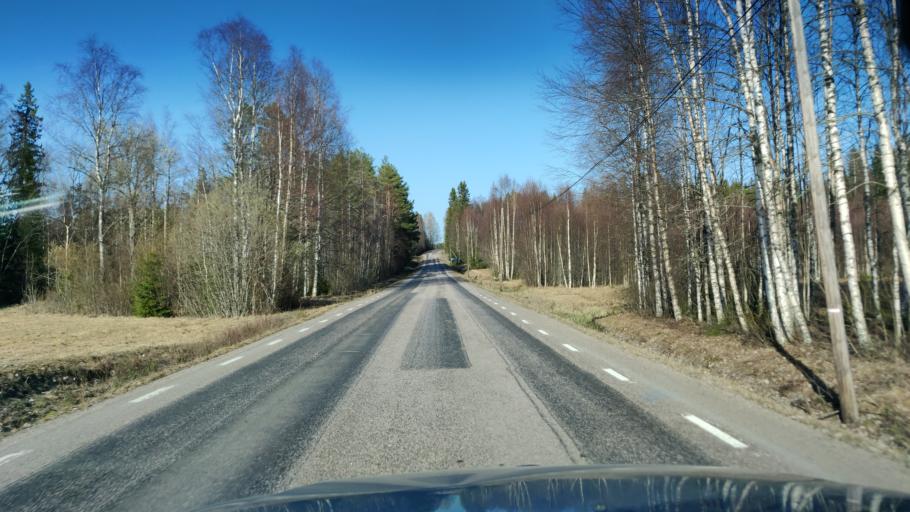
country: SE
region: Vaermland
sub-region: Sunne Kommun
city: Sunne
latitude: 59.9907
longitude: 13.2756
